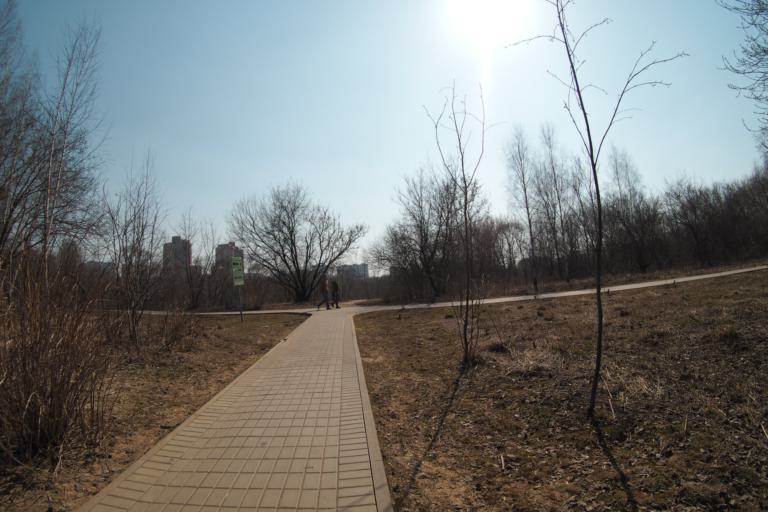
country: RU
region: Moscow
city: Davydkovo
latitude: 55.7163
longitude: 37.4667
